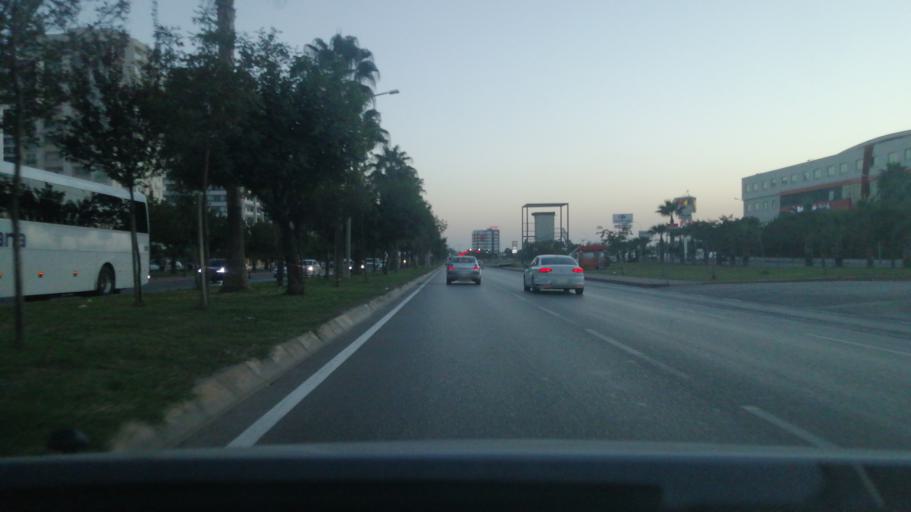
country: TR
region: Adana
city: Seyhan
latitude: 37.0199
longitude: 35.2524
